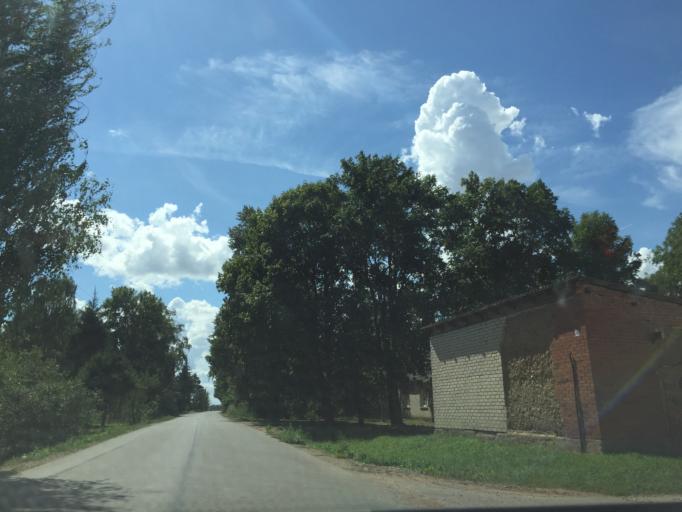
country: LV
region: Rundales
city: Pilsrundale
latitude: 56.3145
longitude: 23.9110
